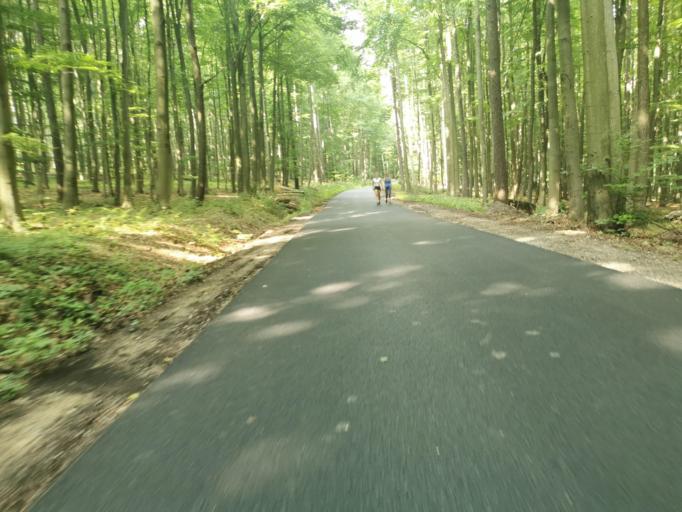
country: SK
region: Trenciansky
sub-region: Okres Myjava
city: Myjava
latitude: 48.7995
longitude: 17.6022
